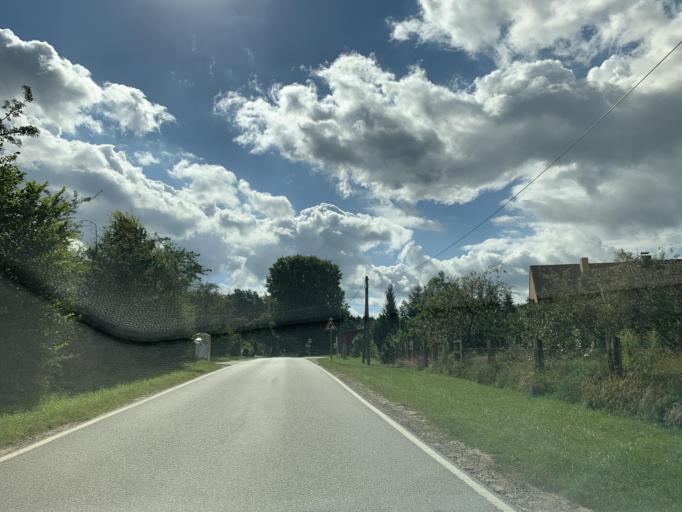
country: DE
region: Mecklenburg-Vorpommern
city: Neustrelitz
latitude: 53.4009
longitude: 13.1270
